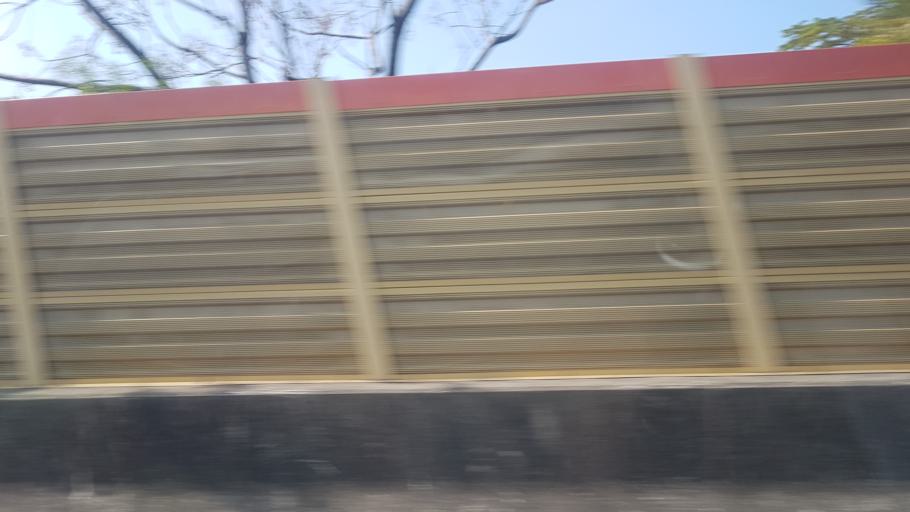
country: TW
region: Taiwan
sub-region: Tainan
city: Tainan
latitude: 22.9857
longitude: 120.2481
